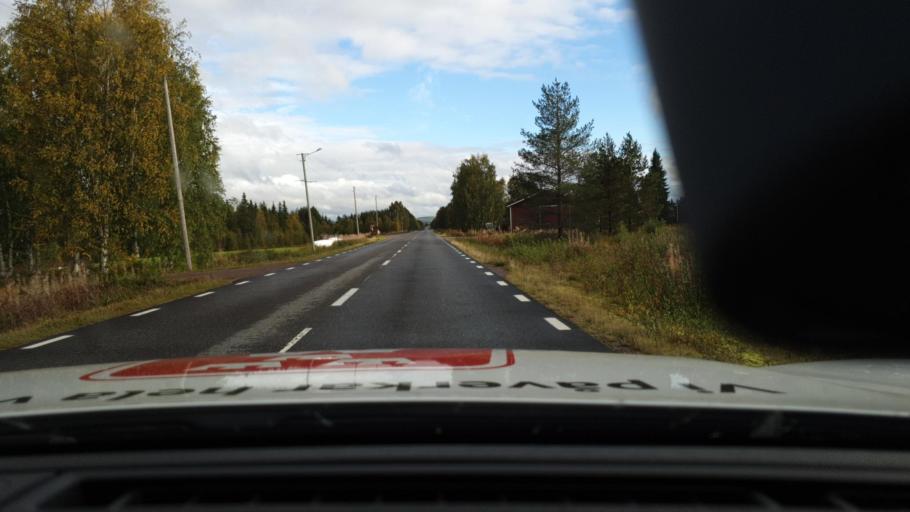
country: SE
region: Norrbotten
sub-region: Overkalix Kommun
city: OEverkalix
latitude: 66.9529
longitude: 22.7051
